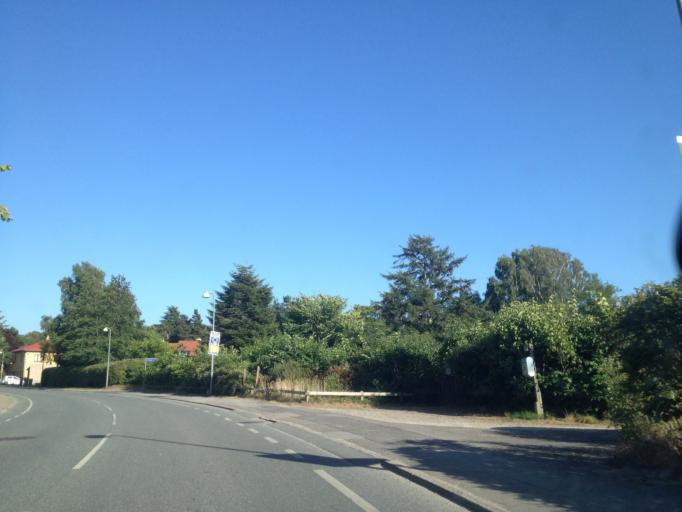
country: DK
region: Capital Region
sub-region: Halsnaes Kommune
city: Frederiksvaerk
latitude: 56.0569
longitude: 12.0806
